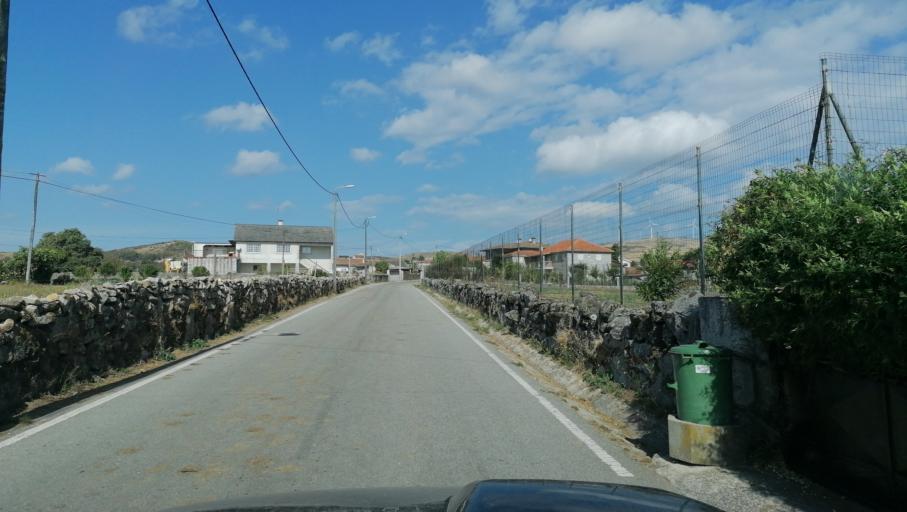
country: PT
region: Vila Real
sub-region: Vila Pouca de Aguiar
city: Vila Pouca de Aguiar
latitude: 41.5215
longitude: -7.6705
